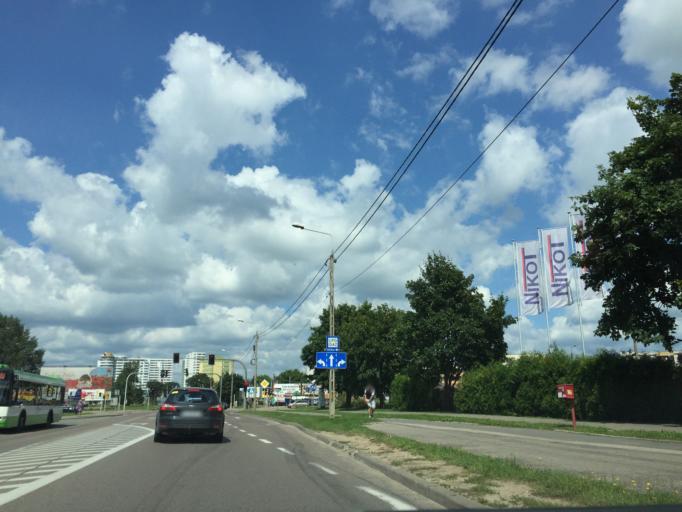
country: PL
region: Podlasie
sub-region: Bialystok
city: Bialystok
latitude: 53.1447
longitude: 23.1575
